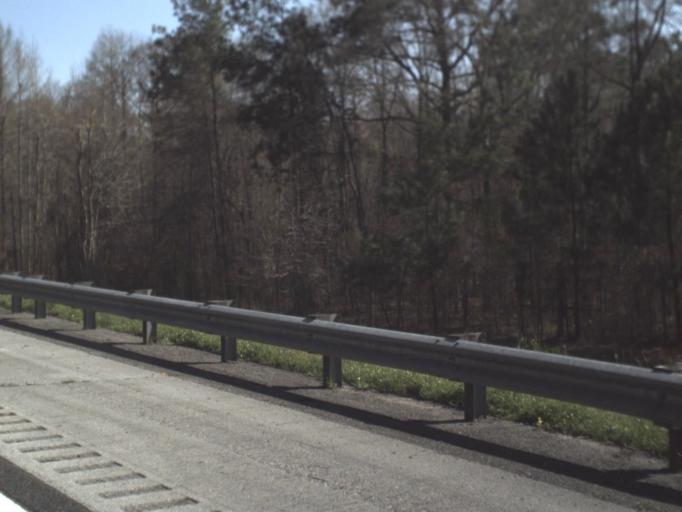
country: US
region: Florida
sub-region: Jackson County
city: Sneads
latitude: 30.6368
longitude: -84.9127
